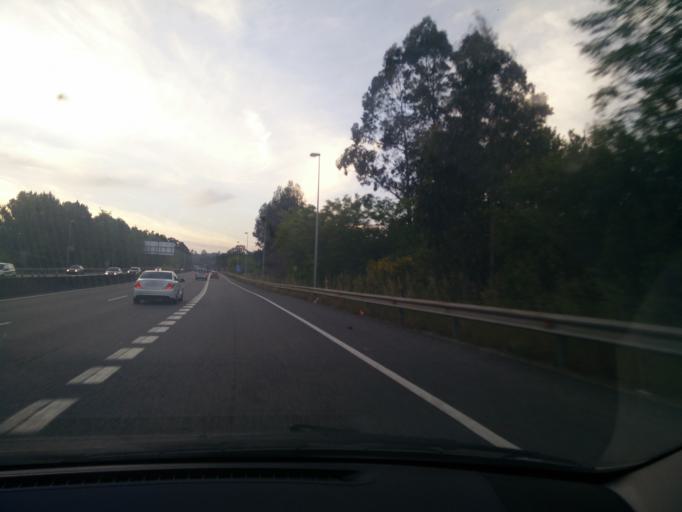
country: ES
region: Galicia
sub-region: Provincia de Pontevedra
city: Porrino
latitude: 42.1734
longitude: -8.6227
